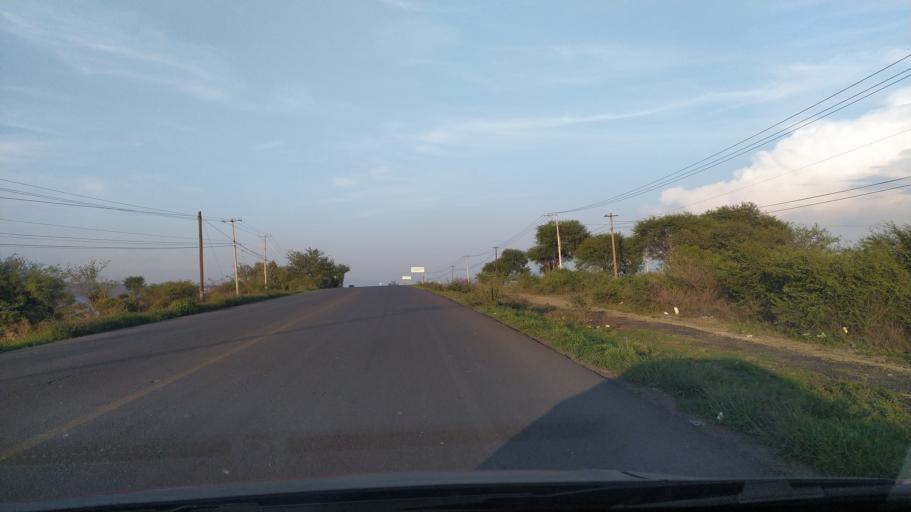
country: MX
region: Michoacan
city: Vistahermosa de Negrete
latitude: 20.2663
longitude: -102.4639
